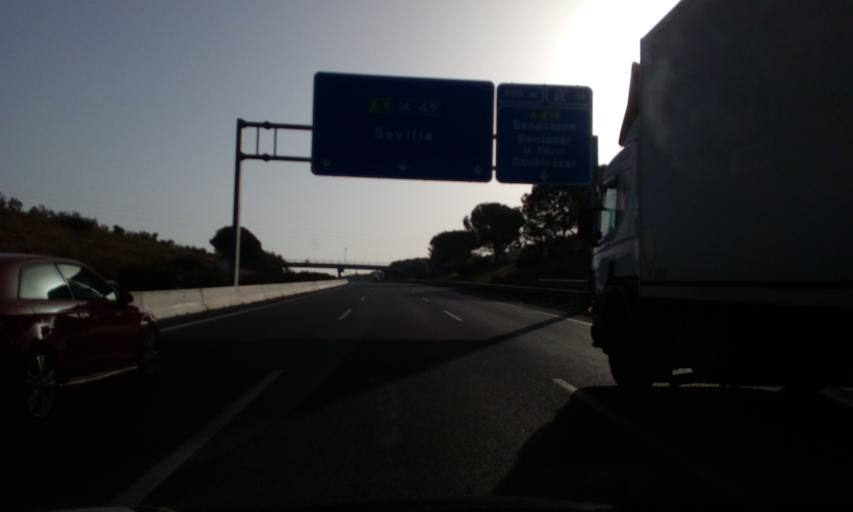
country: ES
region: Andalusia
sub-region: Provincia de Sevilla
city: Benacazon
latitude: 37.3634
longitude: -6.2092
